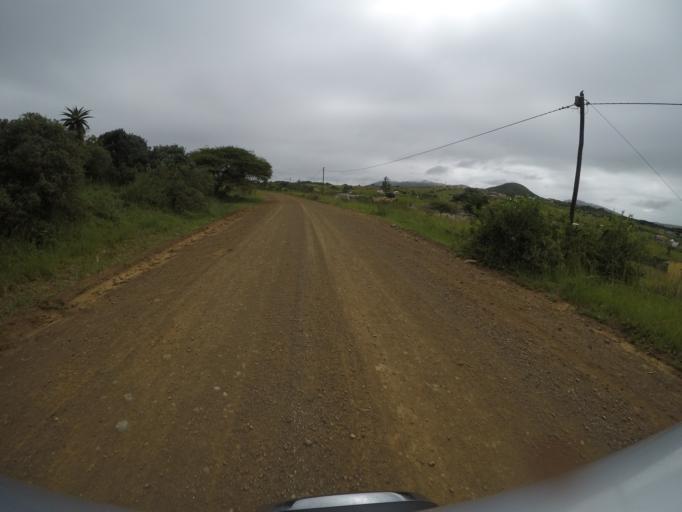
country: ZA
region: KwaZulu-Natal
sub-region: uThungulu District Municipality
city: Empangeni
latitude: -28.6049
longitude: 31.8377
